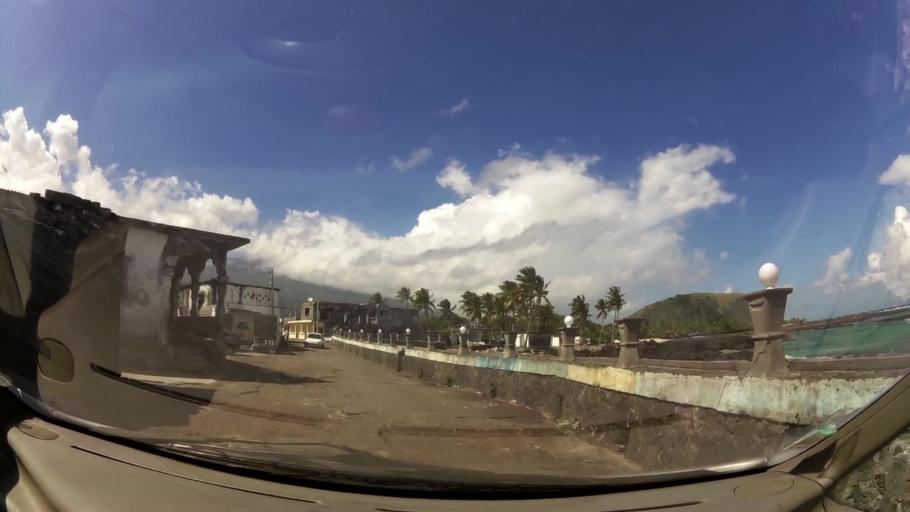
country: KM
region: Grande Comore
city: Mavingouni
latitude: -11.7463
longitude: 43.2315
